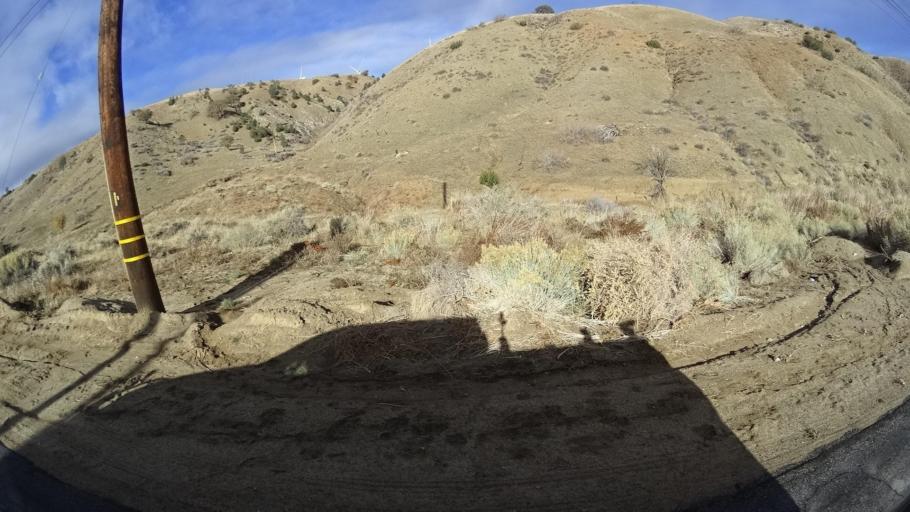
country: US
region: California
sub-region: Kern County
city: Tehachapi
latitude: 35.0895
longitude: -118.3123
